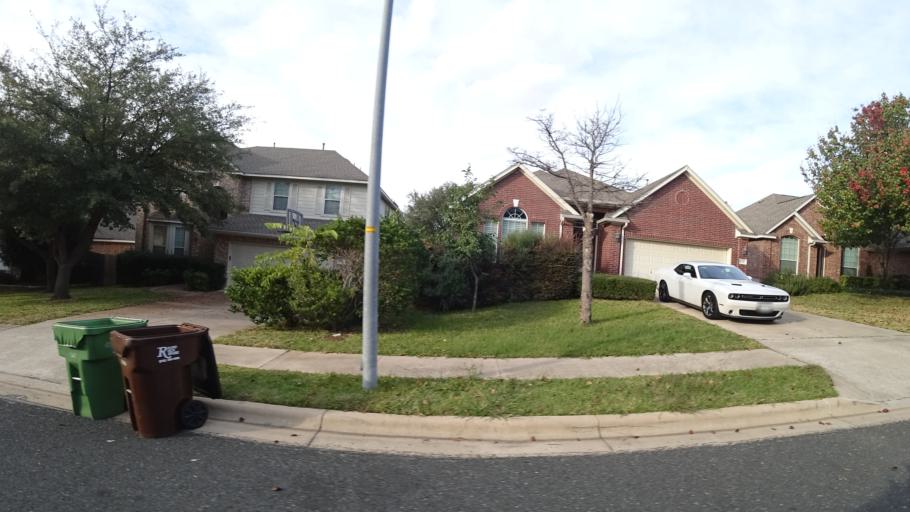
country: US
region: Texas
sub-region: Williamson County
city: Brushy Creek
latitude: 30.5191
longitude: -97.7327
